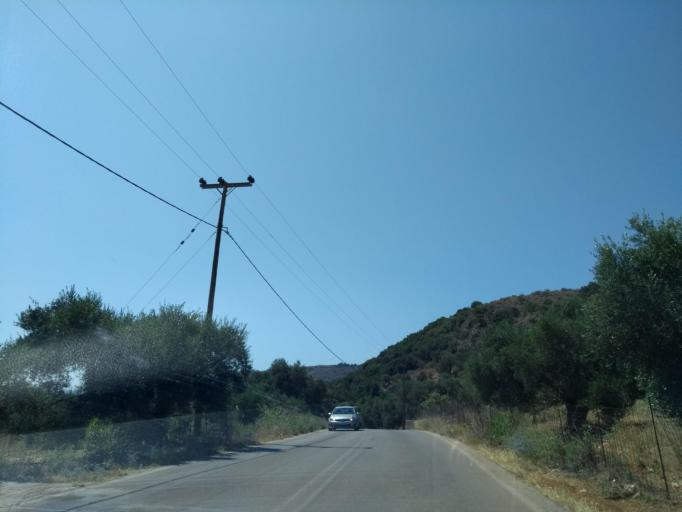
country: GR
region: Crete
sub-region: Nomos Chanias
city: Georgioupolis
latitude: 35.3788
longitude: 24.2442
